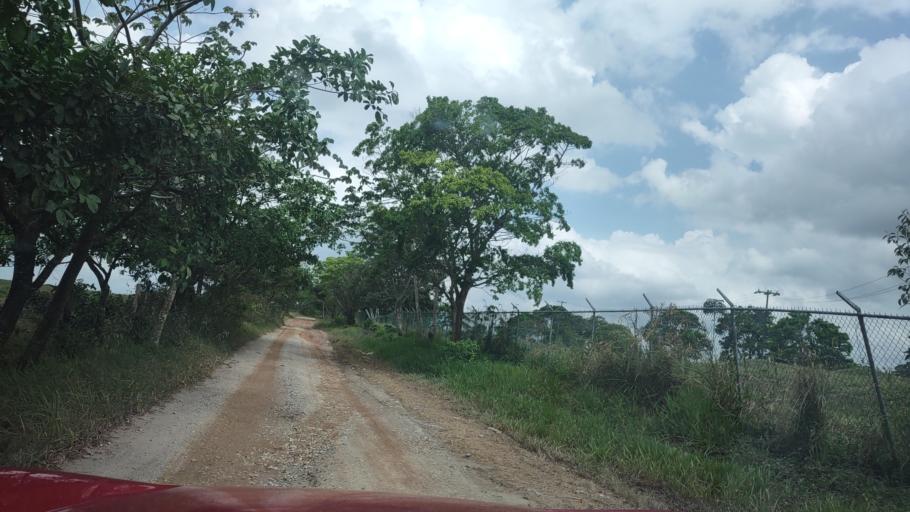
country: MX
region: Veracruz
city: Las Choapas
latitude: 17.9572
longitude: -94.1132
